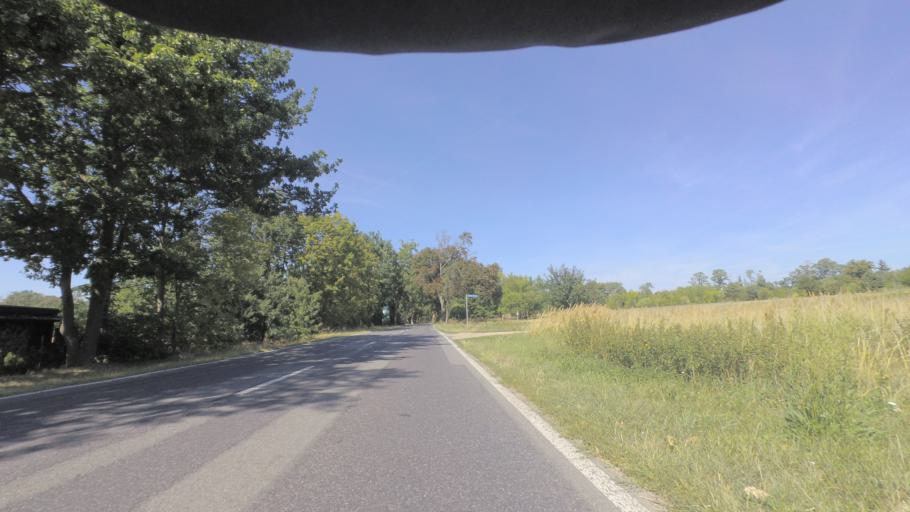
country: DE
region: Brandenburg
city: Am Mellensee
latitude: 52.2485
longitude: 13.3408
